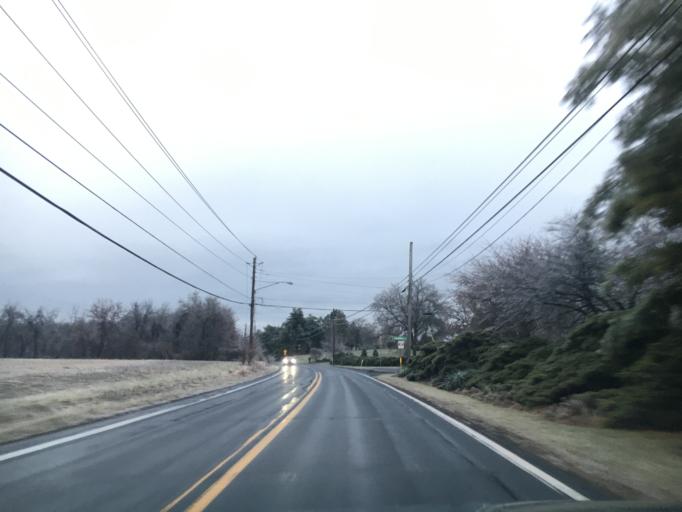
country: US
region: Pennsylvania
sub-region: Lehigh County
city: Schnecksville
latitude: 40.6254
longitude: -75.6207
